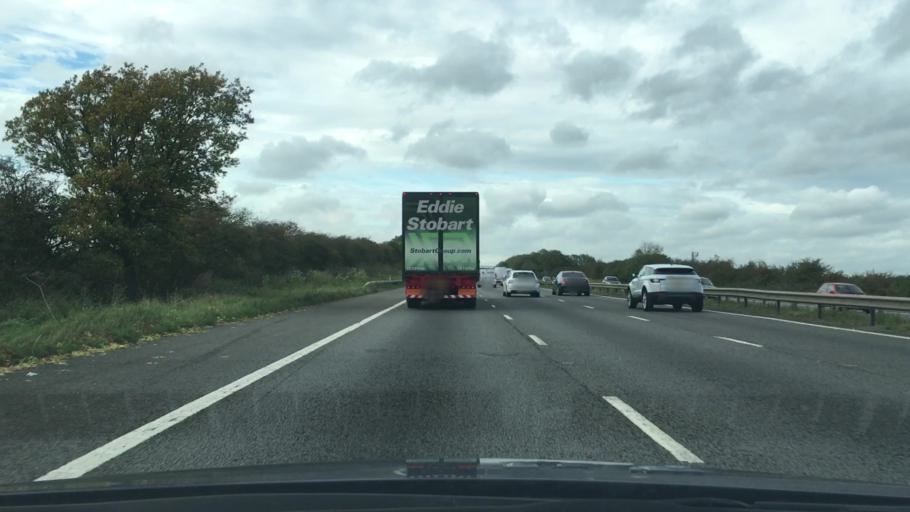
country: GB
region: England
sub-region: Milton Keynes
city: Hanslope
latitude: 52.1282
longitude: -0.8190
